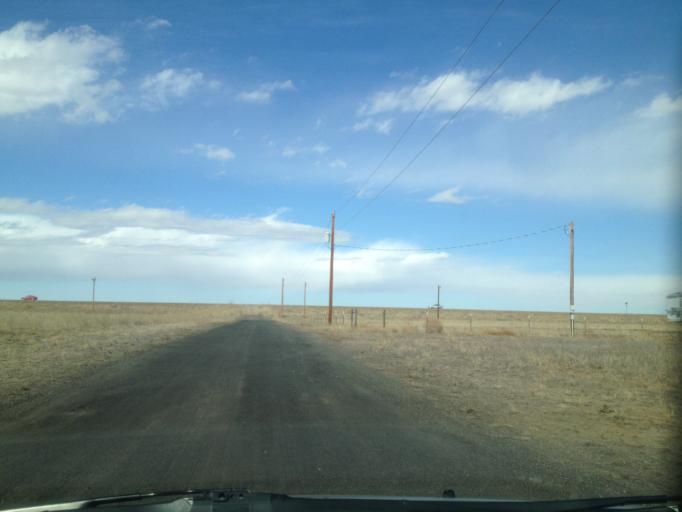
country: US
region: Colorado
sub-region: Weld County
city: Keenesburg
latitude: 40.2894
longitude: -104.2625
